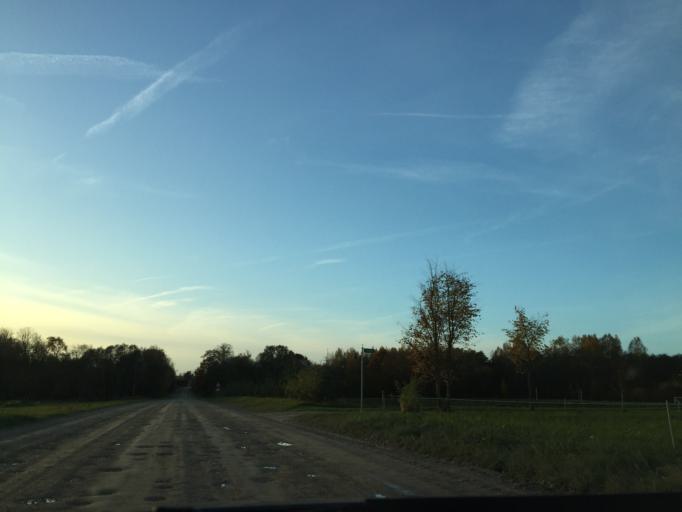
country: LV
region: Malpils
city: Malpils
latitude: 56.8828
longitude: 24.9715
